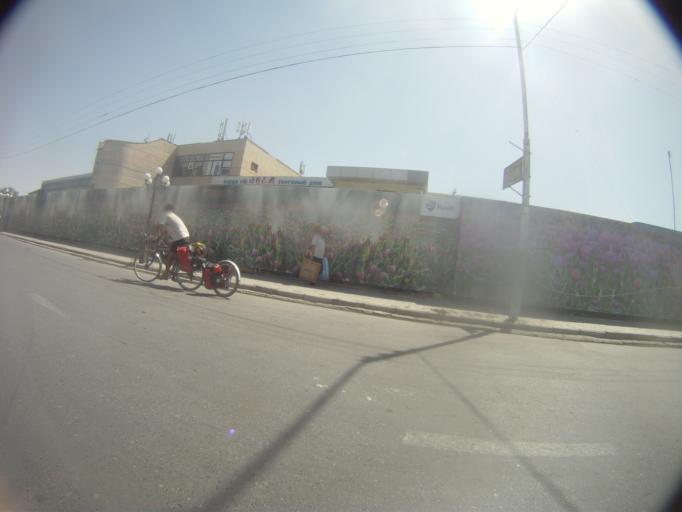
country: KZ
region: Ongtustik Qazaqstan
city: Turkestan
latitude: 43.3010
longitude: 68.2445
